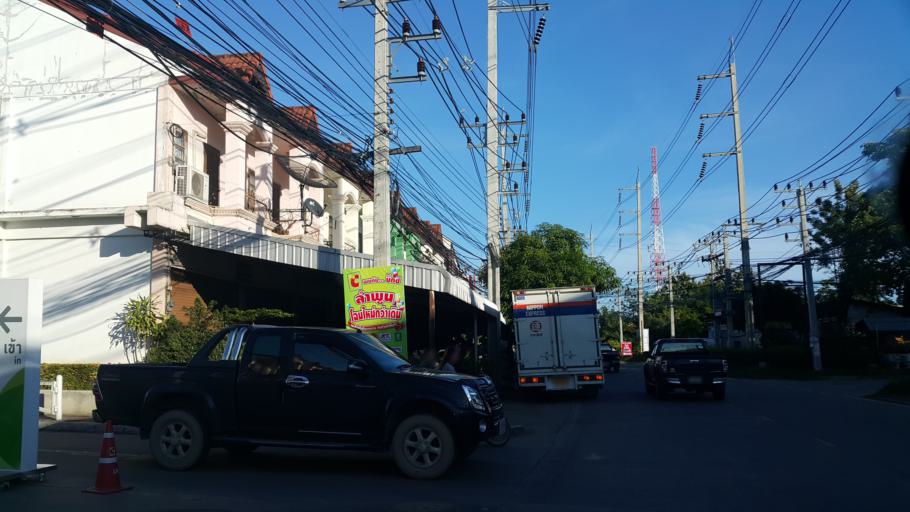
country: TH
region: Lamphun
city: Lamphun
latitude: 18.5903
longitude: 99.0398
